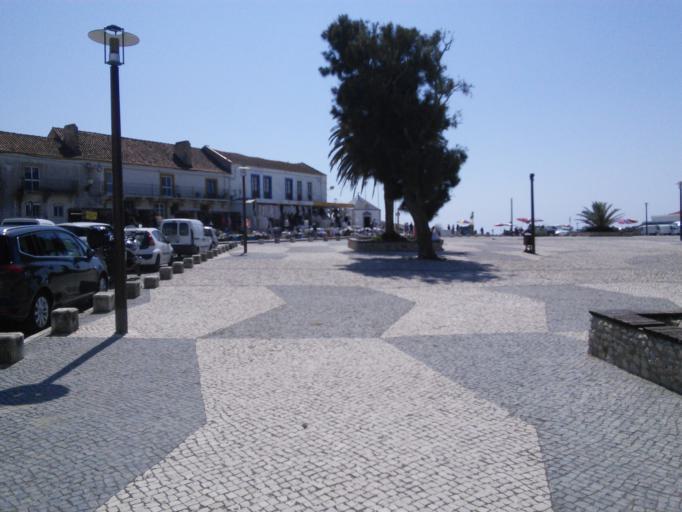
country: PT
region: Leiria
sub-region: Nazare
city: Nazare
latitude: 39.6053
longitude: -9.0758
